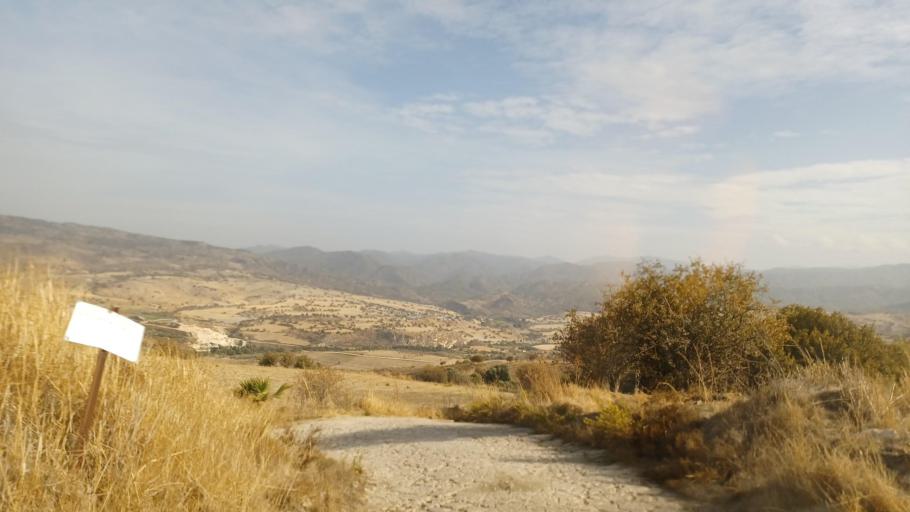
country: CY
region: Pafos
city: Polis
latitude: 34.9409
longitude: 32.5163
